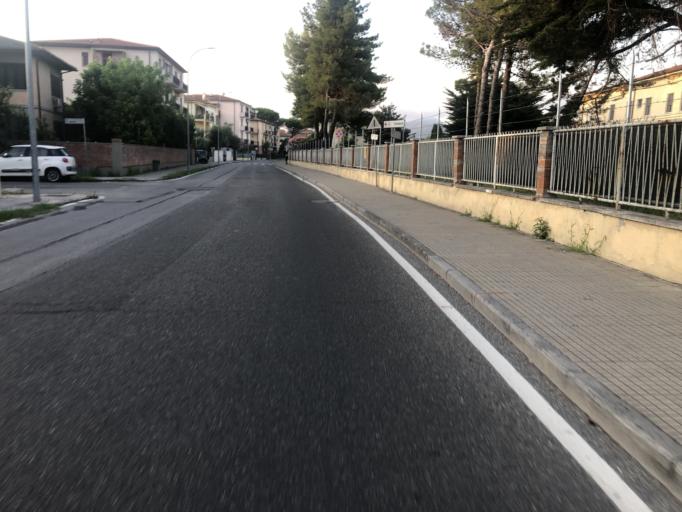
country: IT
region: Tuscany
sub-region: Province of Pisa
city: Pisa
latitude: 43.7302
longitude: 10.4071
